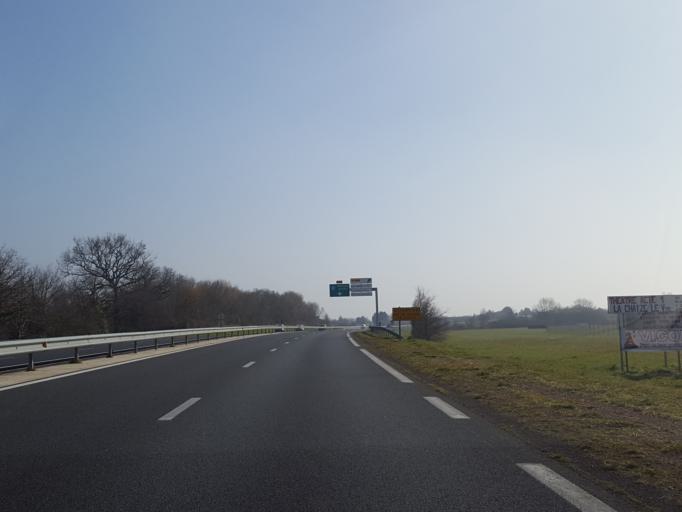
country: FR
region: Pays de la Loire
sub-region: Departement de la Vendee
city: La Chaize-le-Vicomte
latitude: 46.6694
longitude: -1.3208
